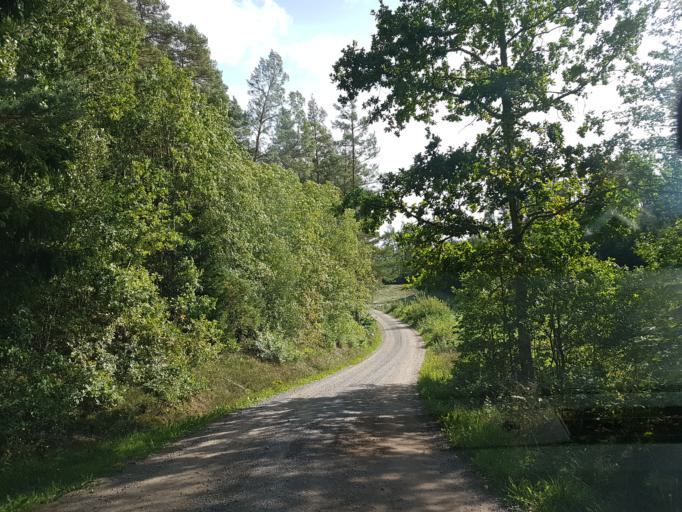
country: SE
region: OEstergoetland
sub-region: Linkopings Kommun
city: Sturefors
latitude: 58.3115
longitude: 15.8455
